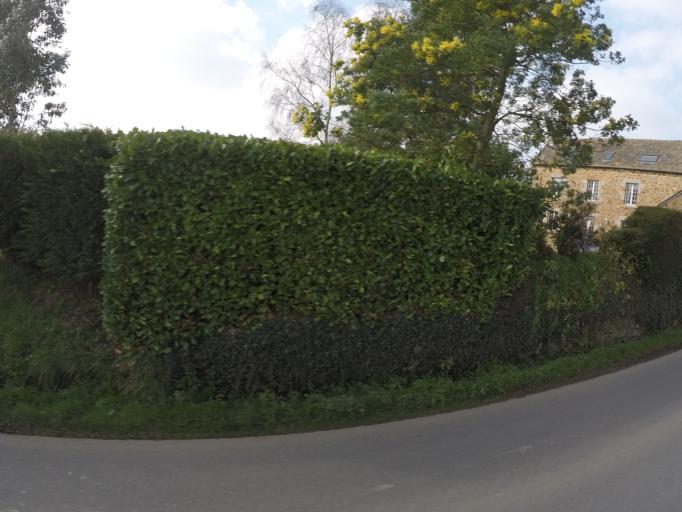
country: FR
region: Brittany
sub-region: Departement des Cotes-d'Armor
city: Goudelin
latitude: 48.6130
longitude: -3.0366
